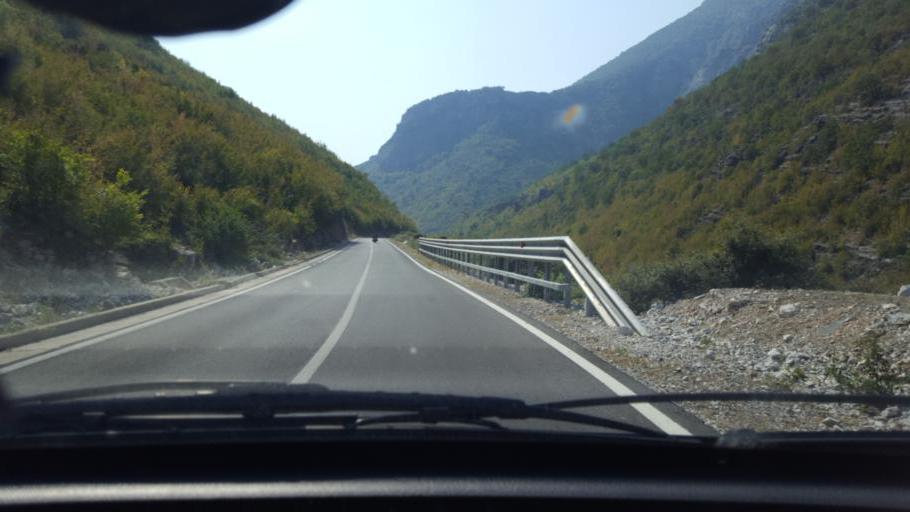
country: AL
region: Shkoder
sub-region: Rrethi i Malesia e Madhe
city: Kastrat
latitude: 42.4485
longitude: 19.5467
